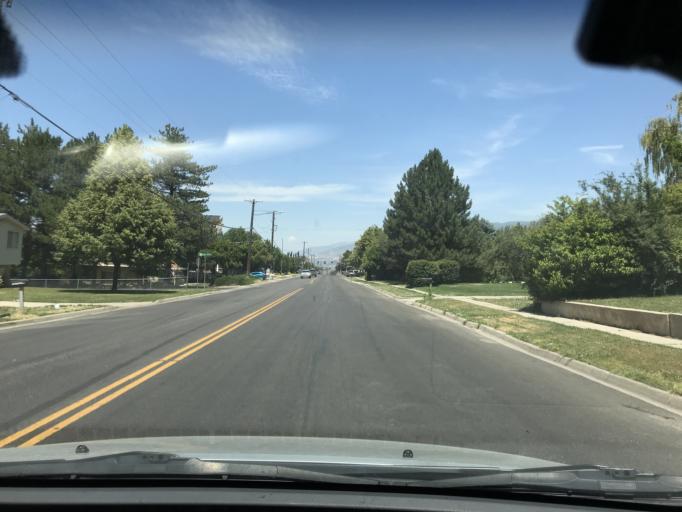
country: US
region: Utah
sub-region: Davis County
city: Woods Cross
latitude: 40.8591
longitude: -111.8922
